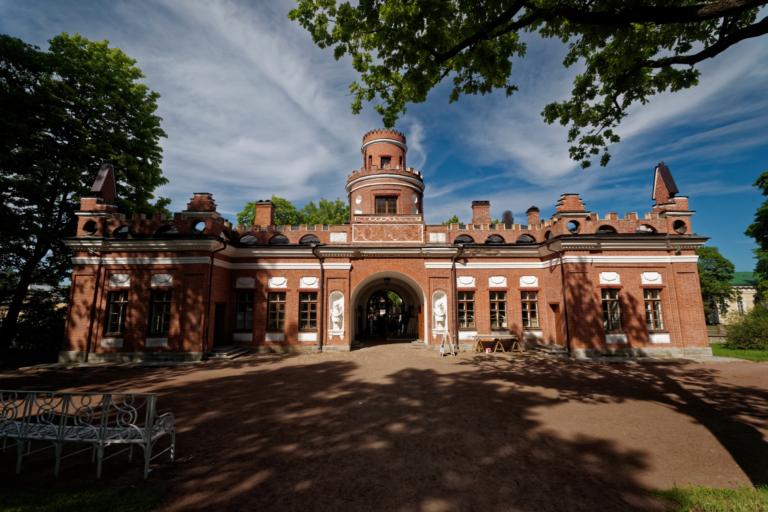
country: RU
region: St.-Petersburg
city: Pushkin
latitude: 59.7144
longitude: 30.4045
